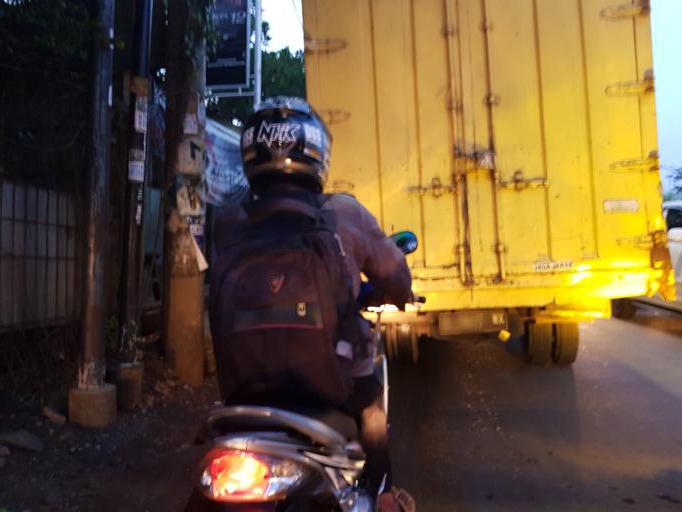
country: ID
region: West Java
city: Serpong
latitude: -6.3308
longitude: 106.6857
